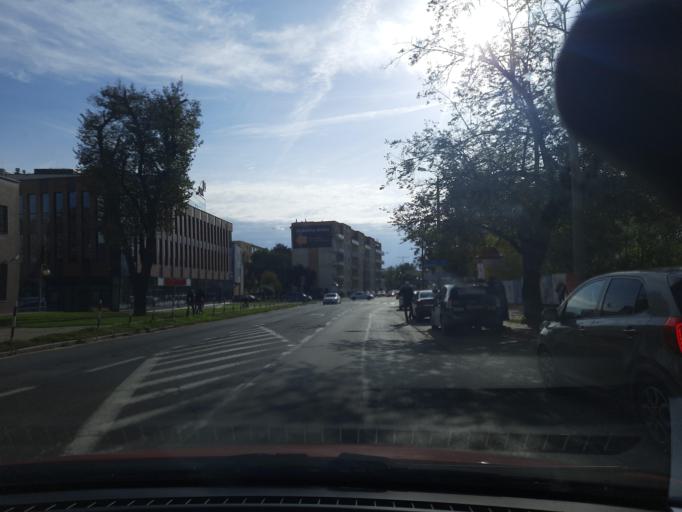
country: PL
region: Kujawsko-Pomorskie
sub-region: Torun
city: Torun
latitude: 53.0171
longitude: 18.6014
